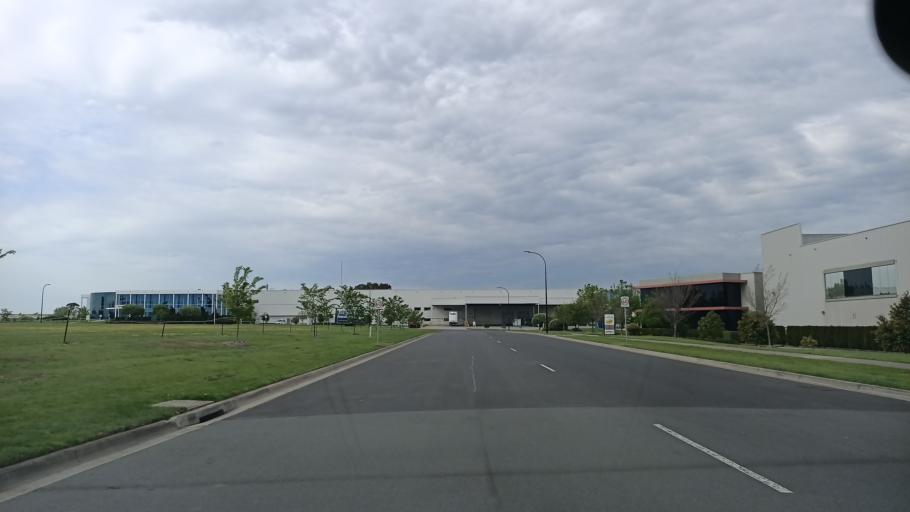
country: AU
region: Victoria
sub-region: Knox
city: Scoresby
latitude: -37.9048
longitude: 145.2228
